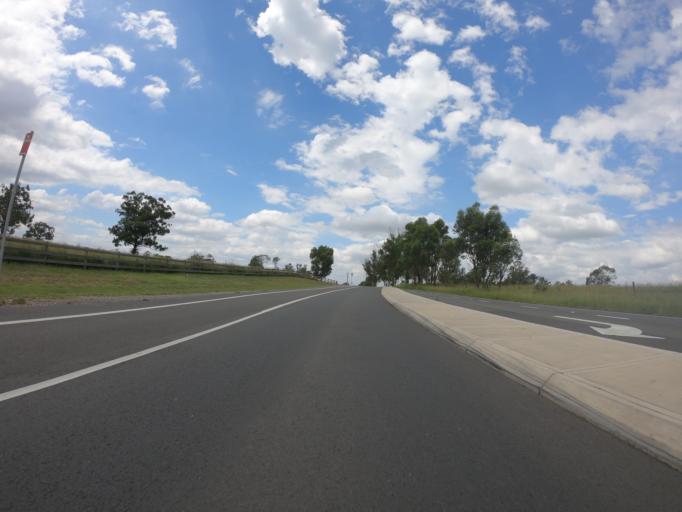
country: AU
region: New South Wales
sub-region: Liverpool
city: Luddenham
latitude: -33.8408
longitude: 150.7432
